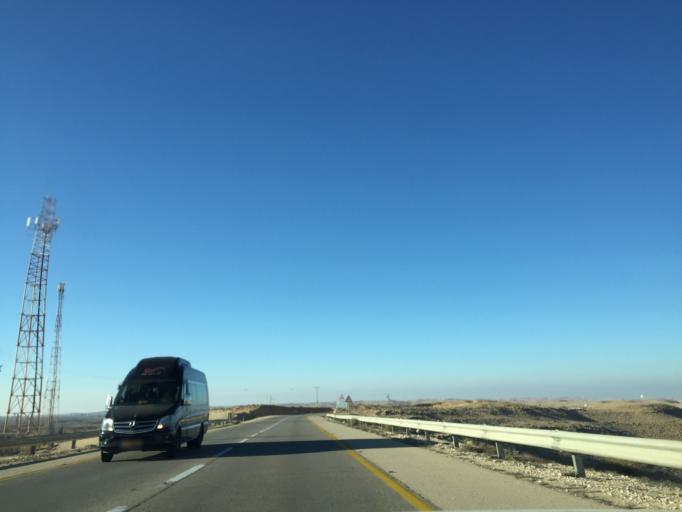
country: IL
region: Southern District
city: Midreshet Ben-Gurion
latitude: 30.7306
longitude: 34.7722
